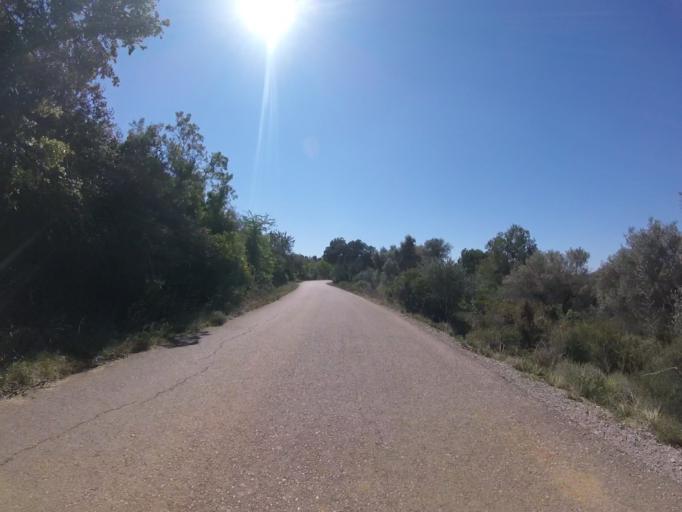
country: ES
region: Valencia
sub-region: Provincia de Castello
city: Cuevas de Vinroma
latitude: 40.3942
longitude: 0.1626
